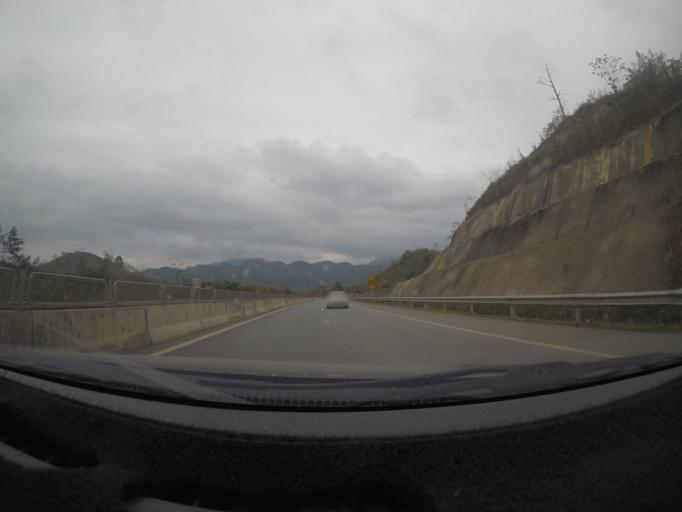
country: VN
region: Lao Cai
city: Thi Tran Khanh Yen
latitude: 22.1521
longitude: 104.3583
